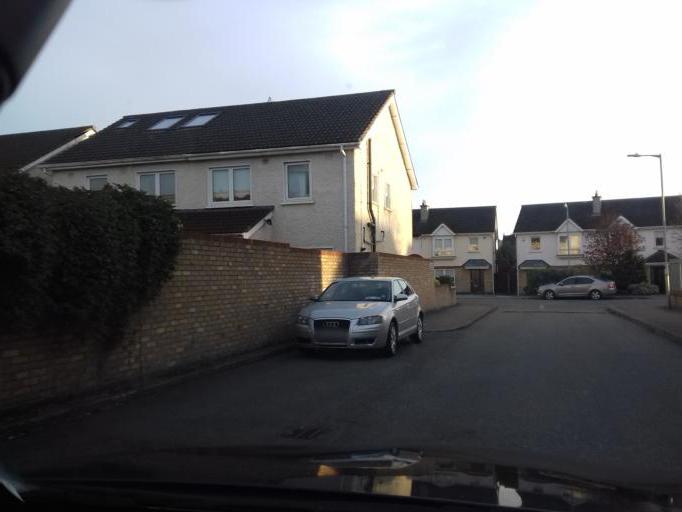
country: IE
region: Leinster
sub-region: Fingal County
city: Blanchardstown
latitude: 53.3817
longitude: -6.3992
